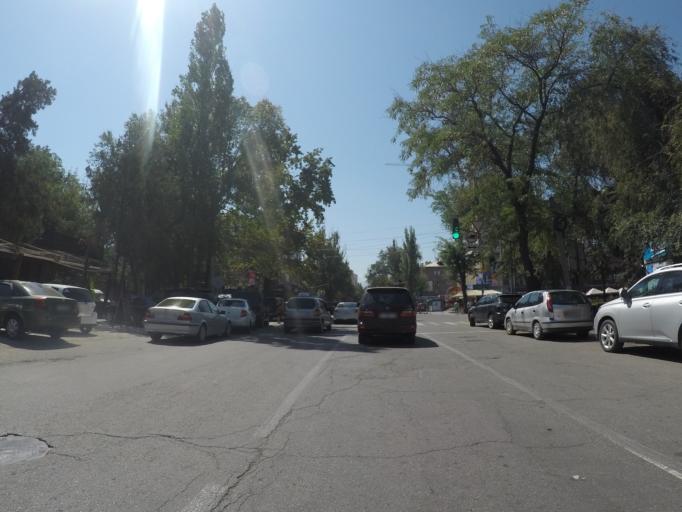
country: KG
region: Chuy
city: Bishkek
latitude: 42.8769
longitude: 74.5917
